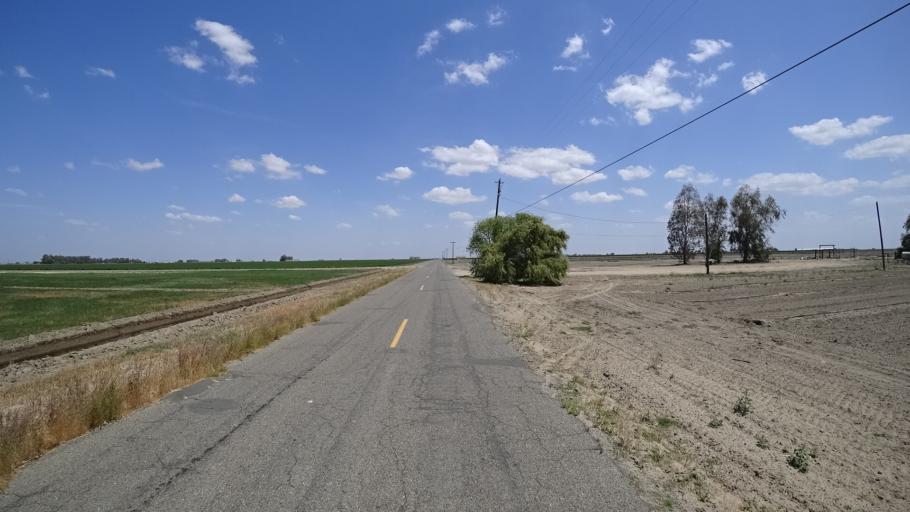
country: US
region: California
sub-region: Kings County
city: Stratford
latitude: 36.1821
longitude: -119.8128
